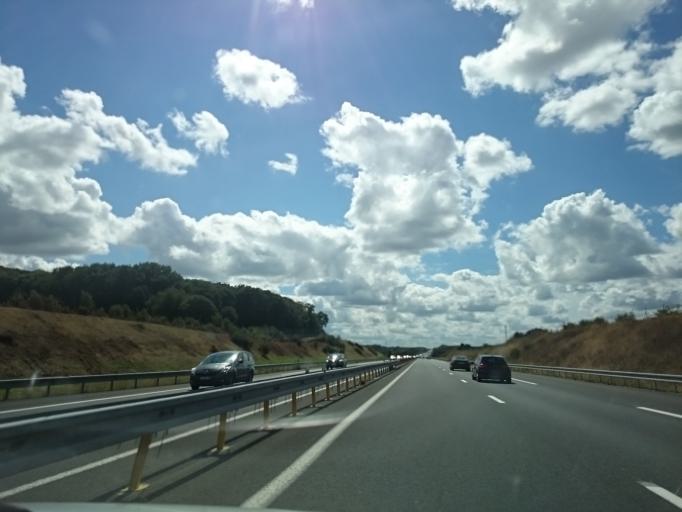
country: FR
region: Pays de la Loire
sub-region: Departement de Maine-et-Loire
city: Saint-Lambert-la-Potherie
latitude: 47.4839
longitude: -0.6627
